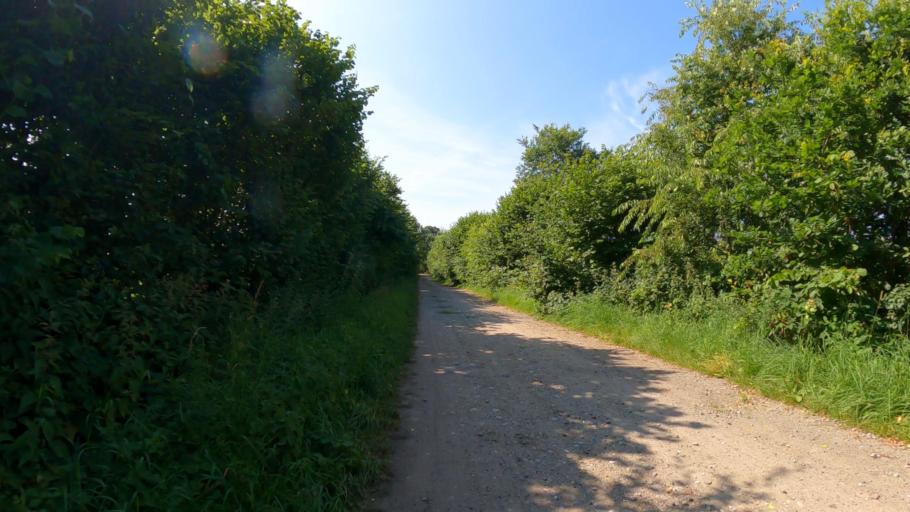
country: DE
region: Schleswig-Holstein
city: Latendorf
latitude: 54.0265
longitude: 10.0600
